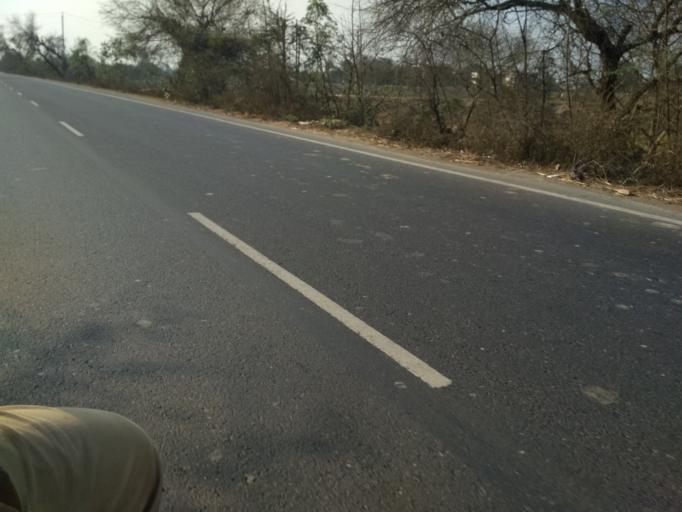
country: IN
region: Bihar
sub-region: Khagaria
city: Khagaria
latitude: 25.5077
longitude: 86.5485
